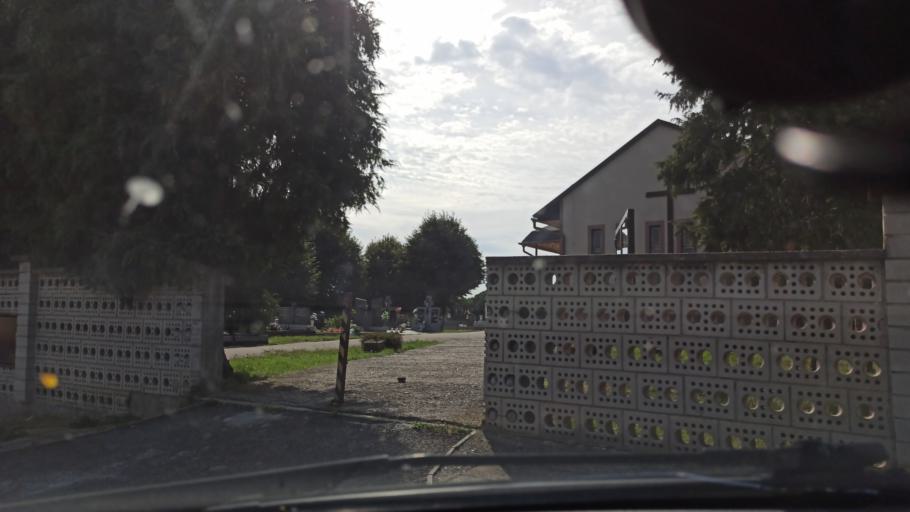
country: SK
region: Trnavsky
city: Gbely
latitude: 48.6824
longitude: 17.1992
